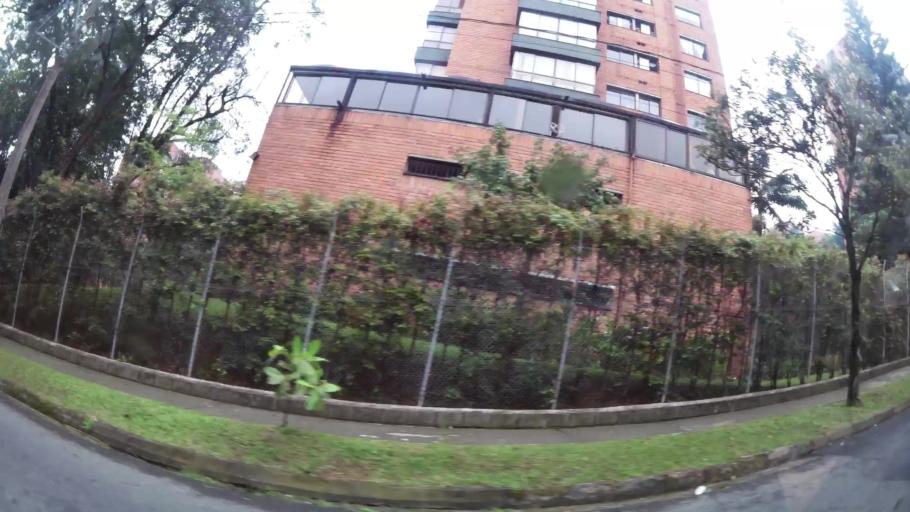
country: CO
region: Antioquia
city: Envigado
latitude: 6.1893
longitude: -75.5670
